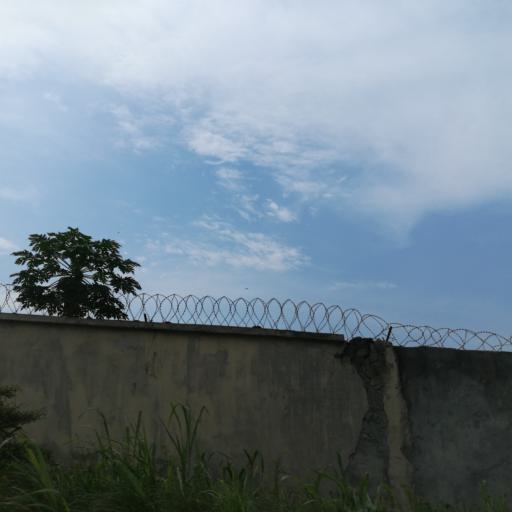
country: NG
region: Rivers
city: Port Harcourt
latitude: 4.8489
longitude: 7.0151
